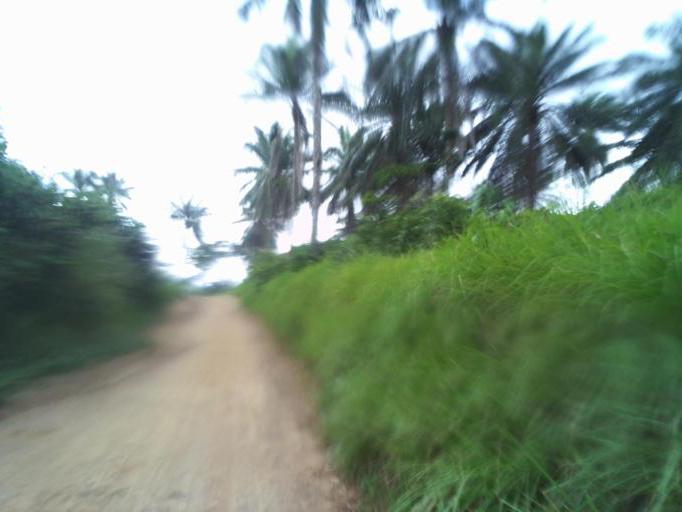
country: SL
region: Eastern Province
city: Kenema
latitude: 7.8348
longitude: -11.1875
